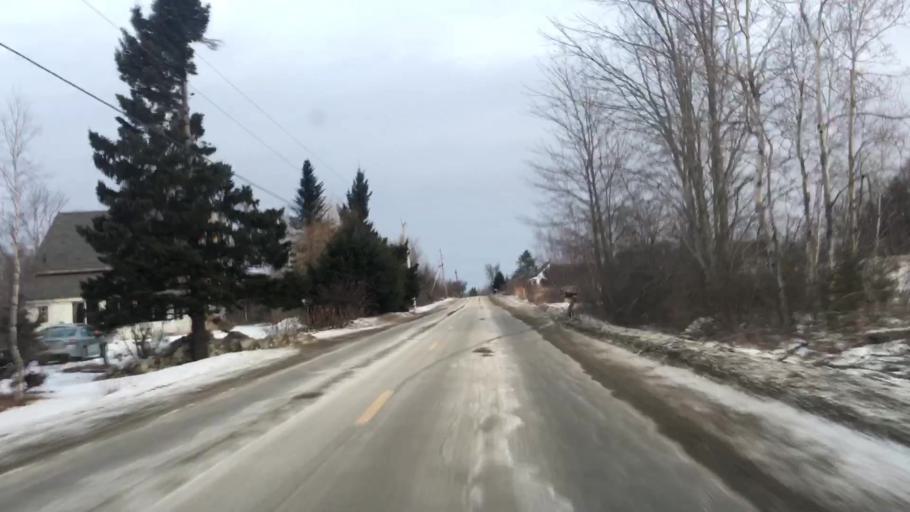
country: US
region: Maine
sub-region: Hancock County
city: Franklin
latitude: 44.7303
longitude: -68.3354
